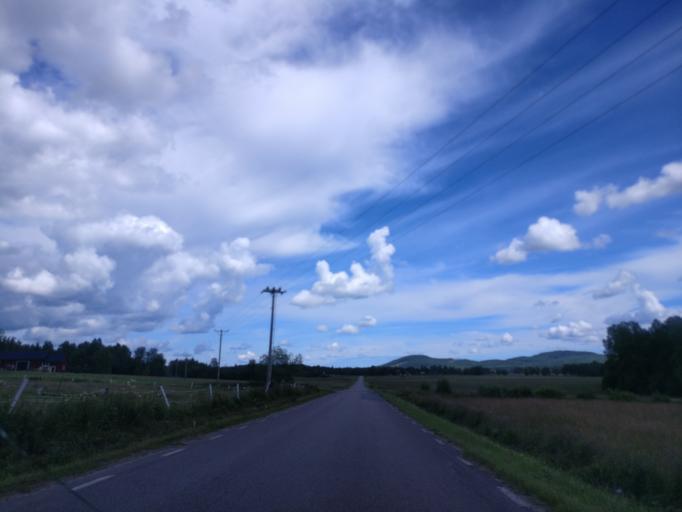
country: SE
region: Vaermland
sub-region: Hagfors Kommun
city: Ekshaerad
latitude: 60.1204
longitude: 13.4522
